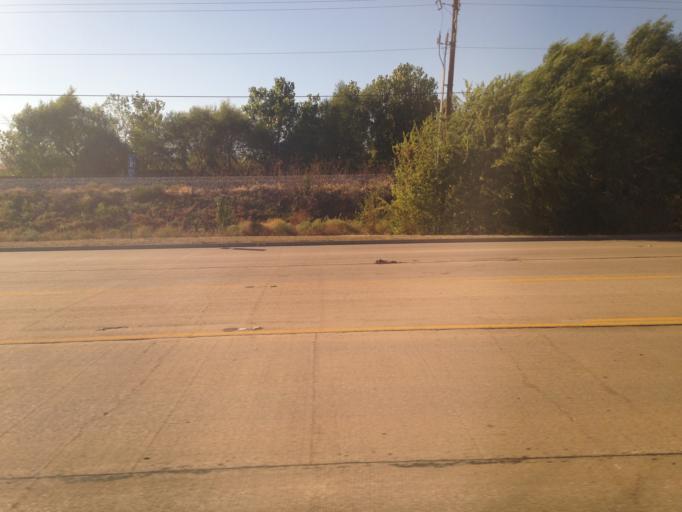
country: US
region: Texas
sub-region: Tarrant County
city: Watauga
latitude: 32.8765
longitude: -97.2615
